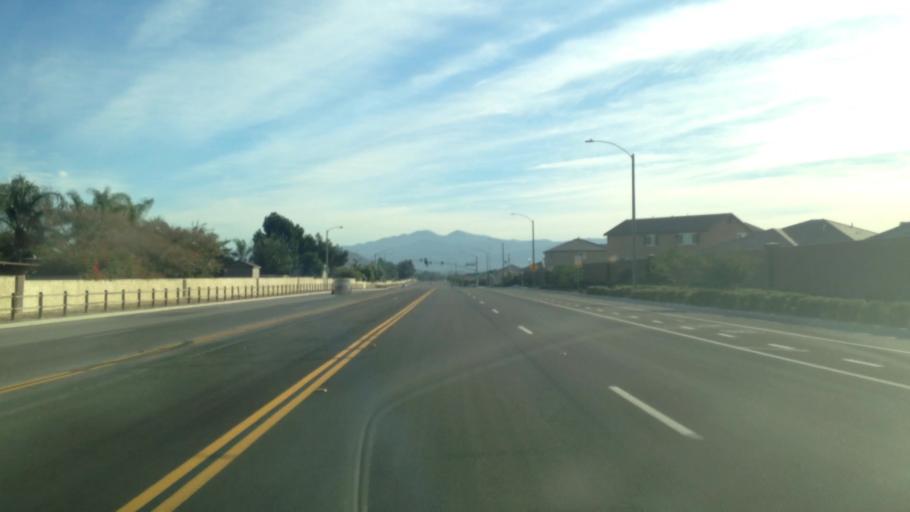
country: US
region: California
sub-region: Riverside County
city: Mira Loma
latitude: 33.9879
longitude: -117.5407
